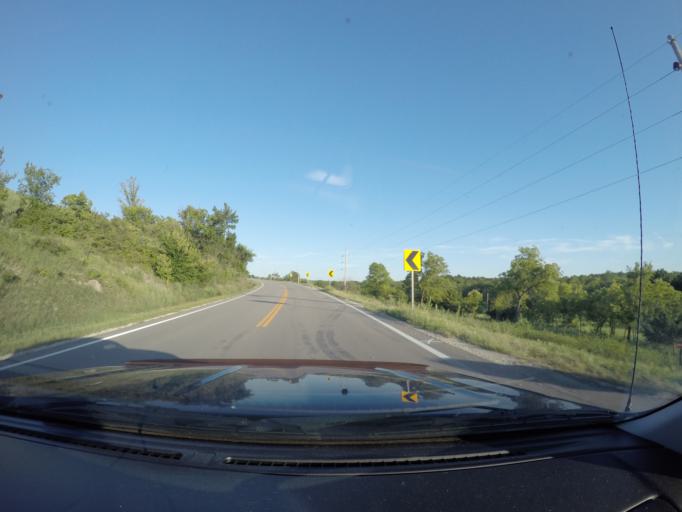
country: US
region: Kansas
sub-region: Pottawatomie County
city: Wamego
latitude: 39.1275
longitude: -96.2980
